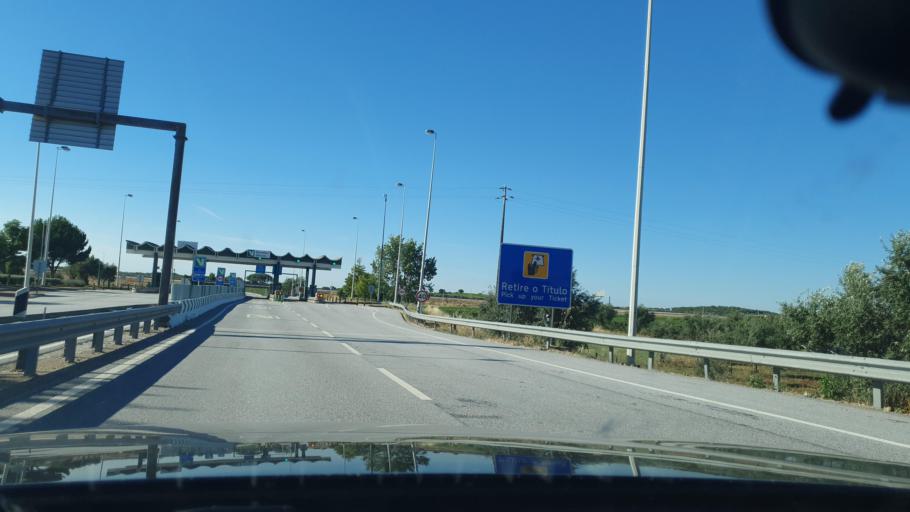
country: PT
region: Evora
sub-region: Borba
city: Borba
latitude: 38.8145
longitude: -7.4740
